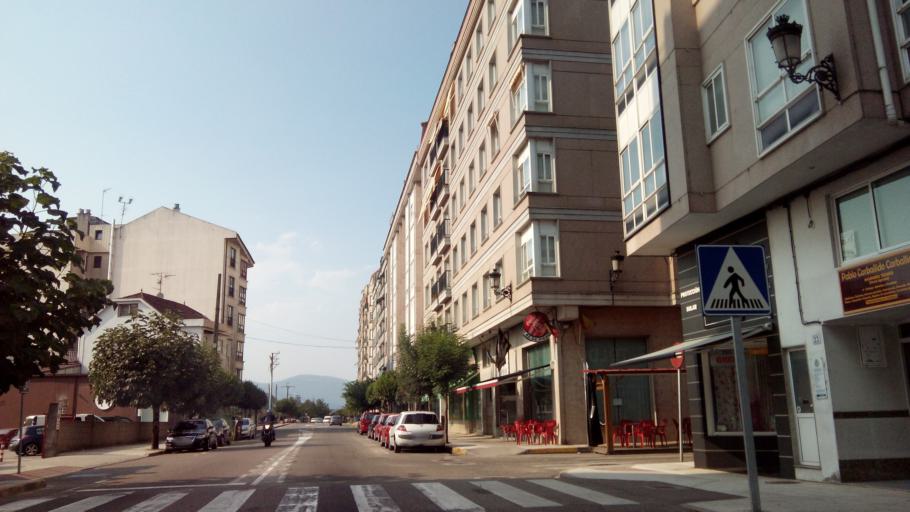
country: ES
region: Galicia
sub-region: Provincia de Pontevedra
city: Ponteareas
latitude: 42.1725
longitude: -8.5085
